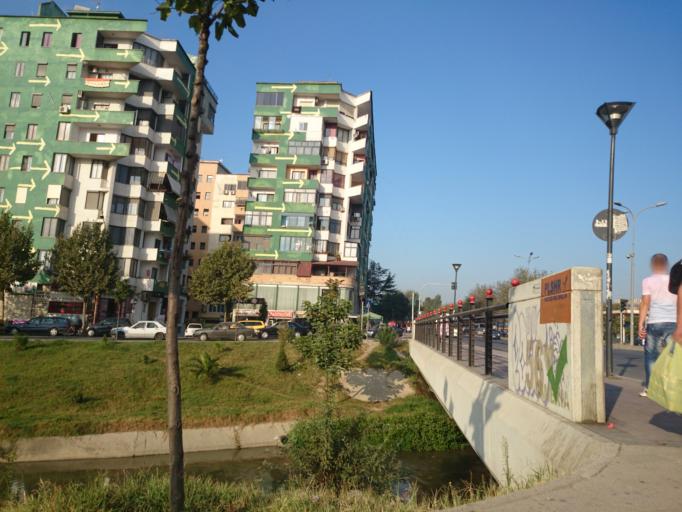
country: AL
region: Tirane
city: Tirana
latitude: 41.3223
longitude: 19.7922
